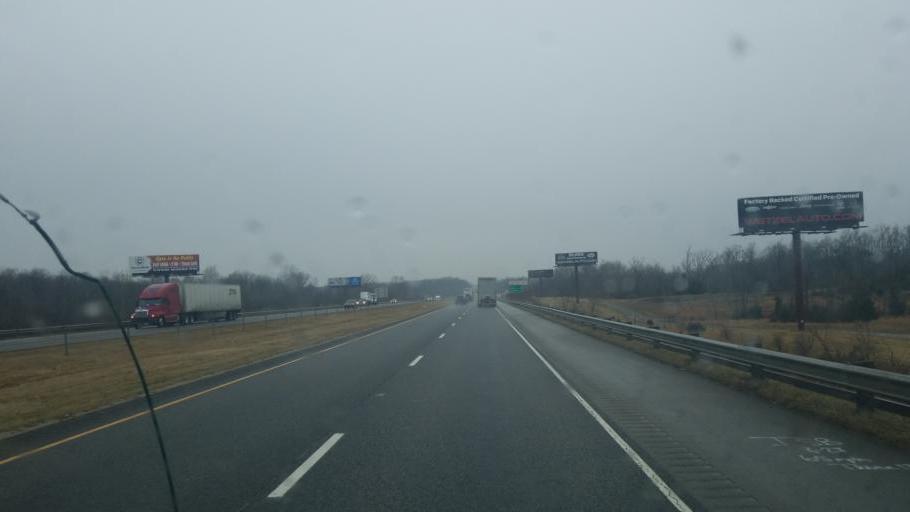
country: US
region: Ohio
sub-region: Preble County
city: New Paris
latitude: 39.8397
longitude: -84.8235
